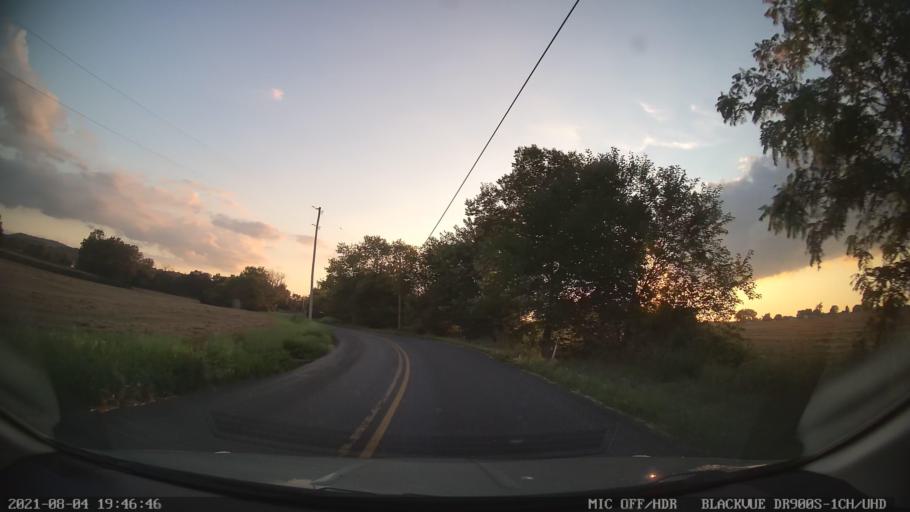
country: US
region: Pennsylvania
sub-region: Lehigh County
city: Breinigsville
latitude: 40.5126
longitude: -75.6616
